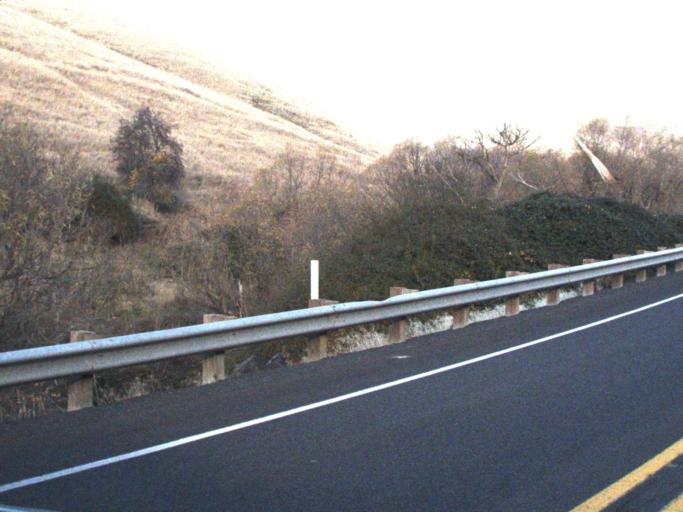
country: US
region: Washington
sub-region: Garfield County
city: Pomeroy
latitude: 46.6653
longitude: -117.7980
